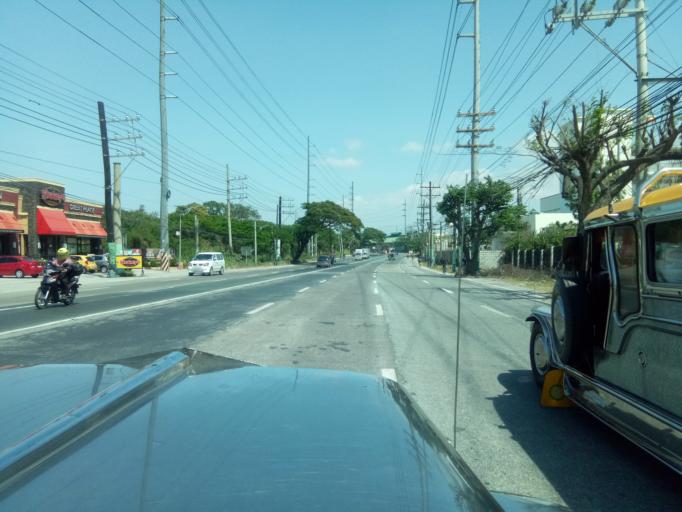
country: PH
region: Calabarzon
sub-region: Province of Cavite
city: Manggahan
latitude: 14.2919
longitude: 120.9242
